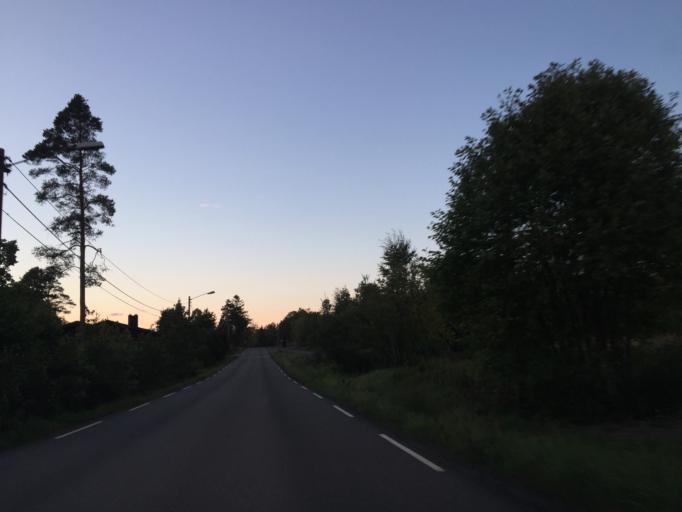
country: NO
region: Ostfold
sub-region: Moss
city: Moss
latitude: 59.5019
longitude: 10.6856
